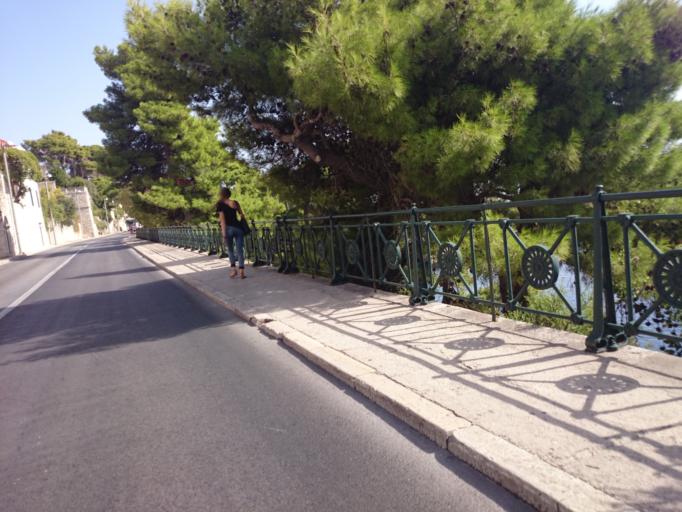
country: HR
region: Dubrovacko-Neretvanska
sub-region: Grad Dubrovnik
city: Dubrovnik
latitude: 42.6460
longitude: 18.0965
